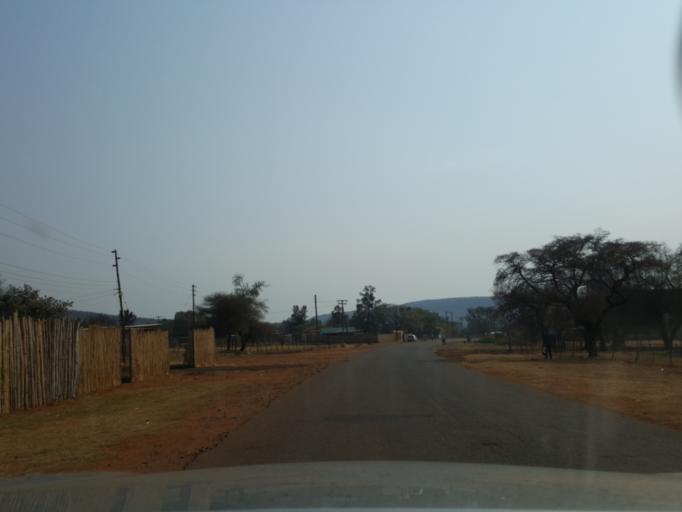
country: BW
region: South East
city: Lobatse
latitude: -25.3158
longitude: 25.7970
